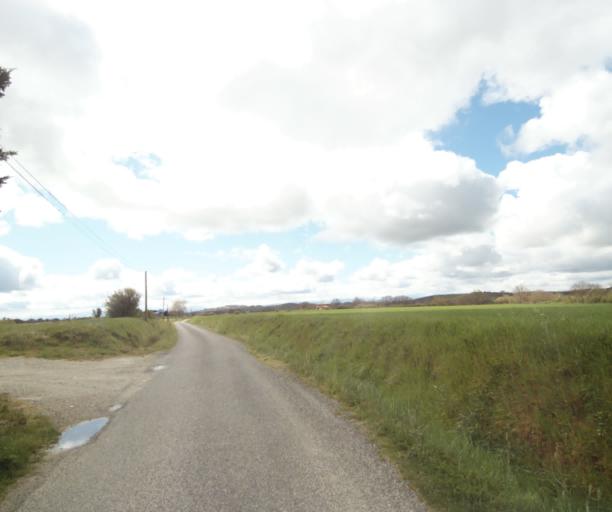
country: FR
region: Midi-Pyrenees
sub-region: Departement de l'Ariege
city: Saverdun
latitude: 43.2239
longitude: 1.5782
